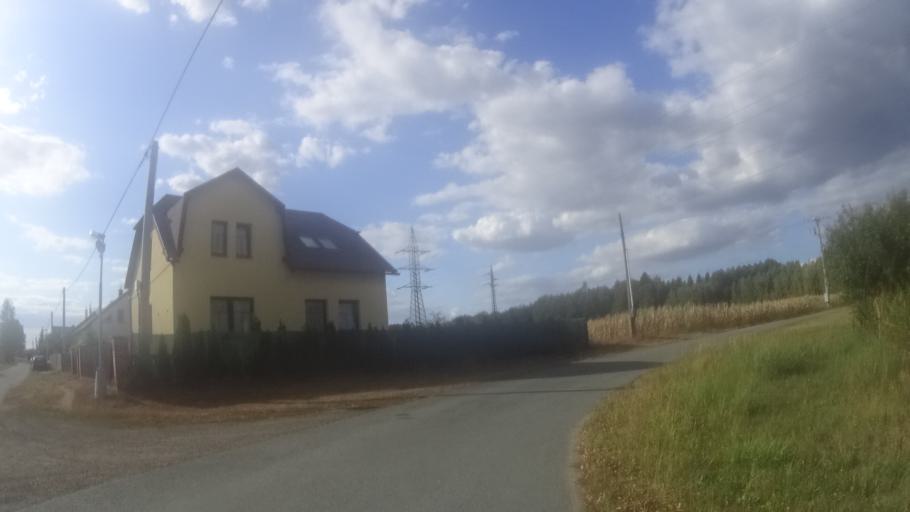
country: CZ
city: Albrechtice nad Orlici
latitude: 50.1730
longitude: 16.0324
